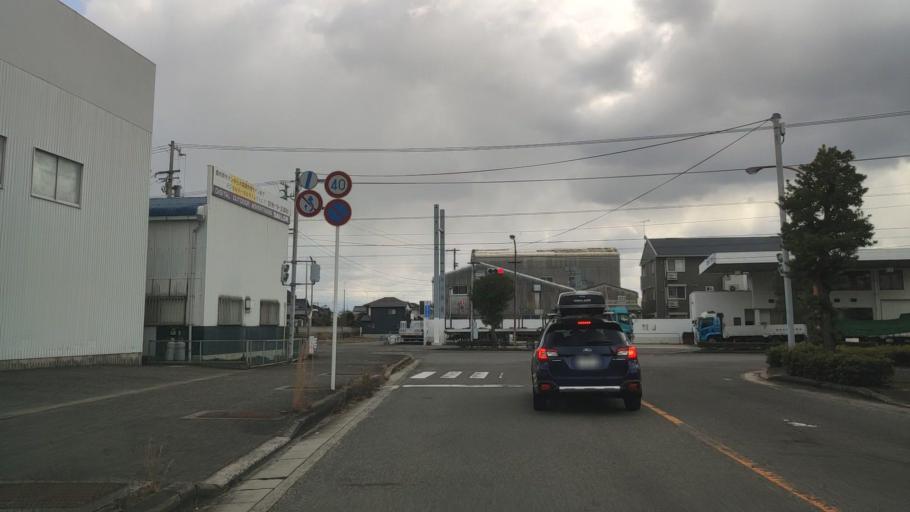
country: JP
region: Ehime
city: Saijo
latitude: 34.0566
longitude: 133.0184
